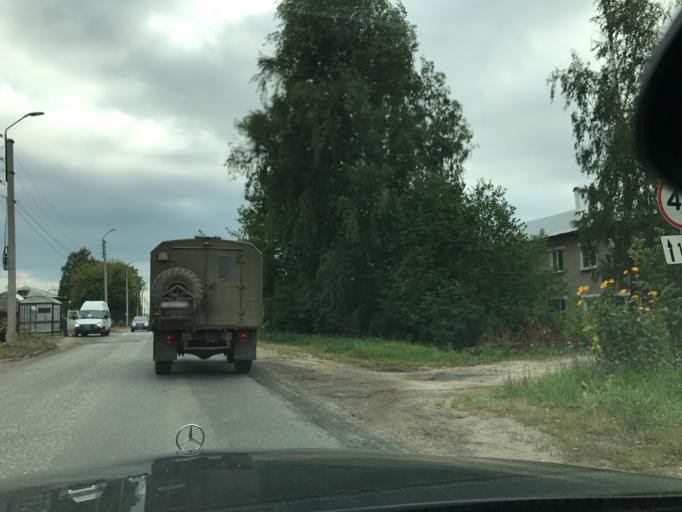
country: RU
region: Vladimir
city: Gorokhovets
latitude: 56.1956
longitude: 42.7076
